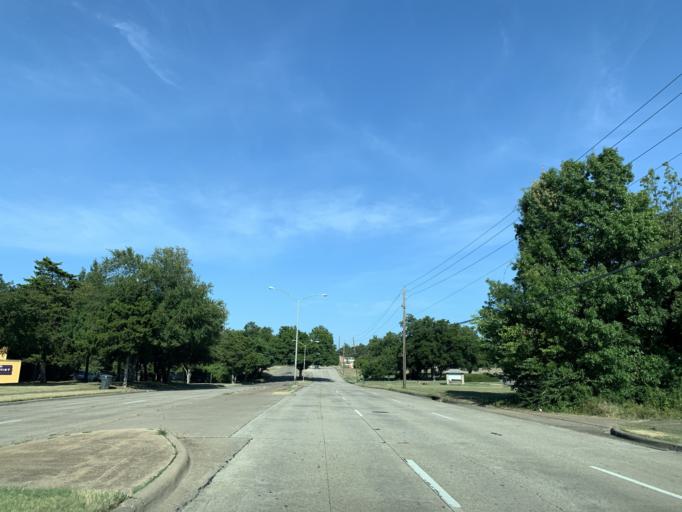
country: US
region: Texas
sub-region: Dallas County
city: Cockrell Hill
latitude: 32.7057
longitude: -96.8852
